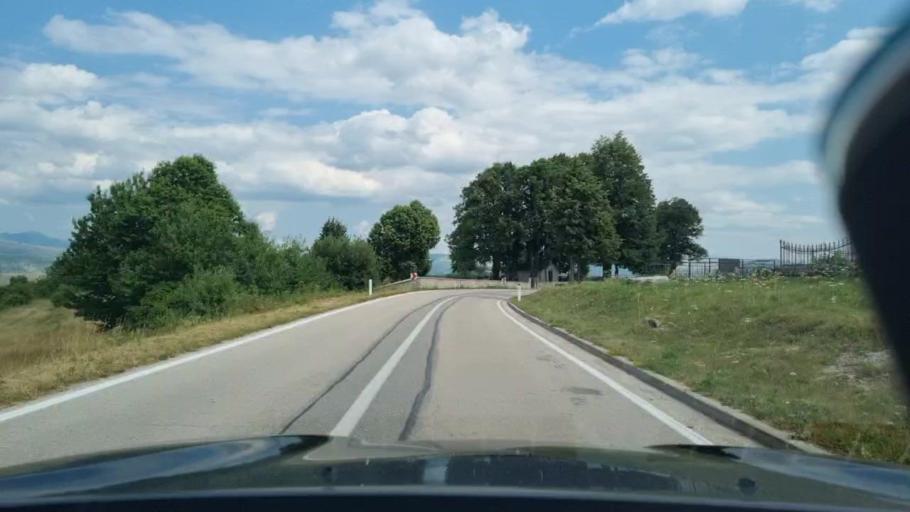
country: BA
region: Federation of Bosnia and Herzegovina
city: Bosansko Grahovo
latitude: 44.1727
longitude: 16.3725
